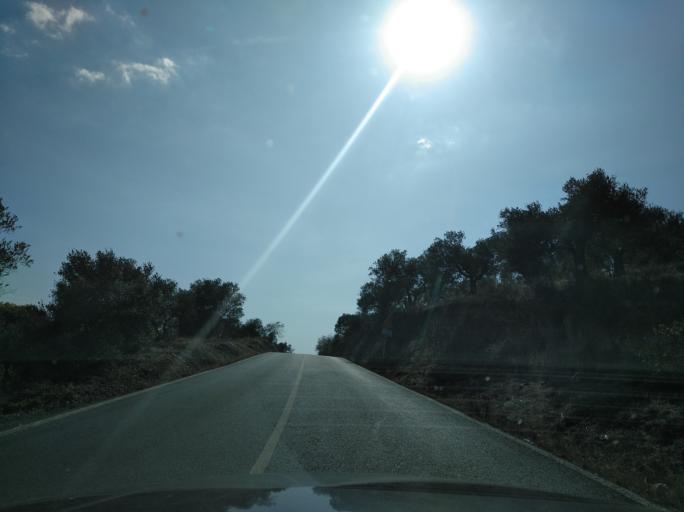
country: ES
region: Andalusia
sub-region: Provincia de Huelva
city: Rosal de la Frontera
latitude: 37.9571
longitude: -7.2655
